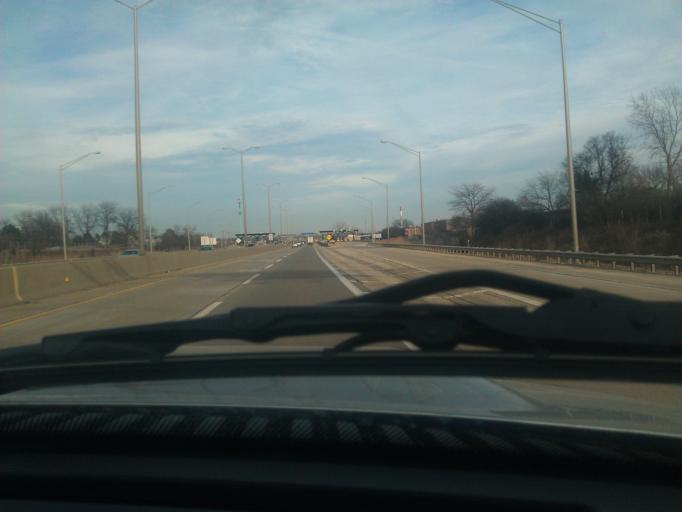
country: US
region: Illinois
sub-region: Lake County
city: Deerfield
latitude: 42.1495
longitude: -87.8614
